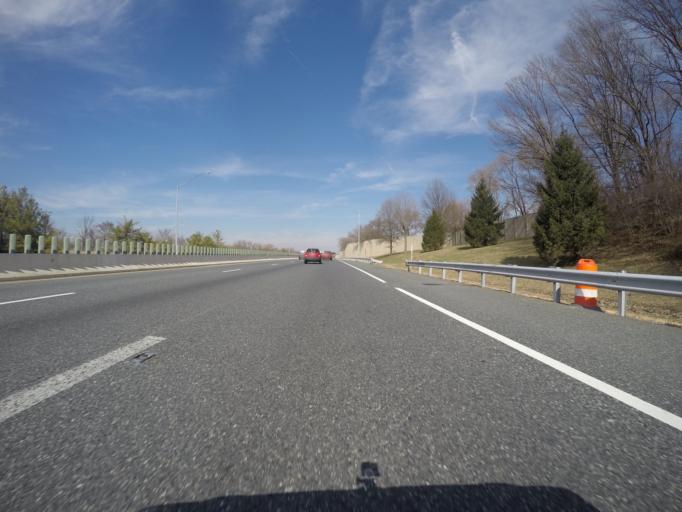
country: US
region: Maryland
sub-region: Anne Arundel County
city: Brooklyn Park
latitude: 39.2293
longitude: -76.6236
